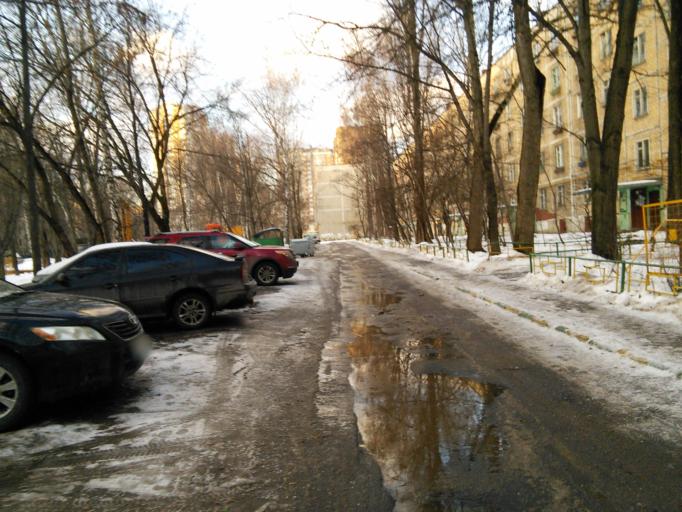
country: RU
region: Moscow
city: Likhobory
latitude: 55.8620
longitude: 37.5604
